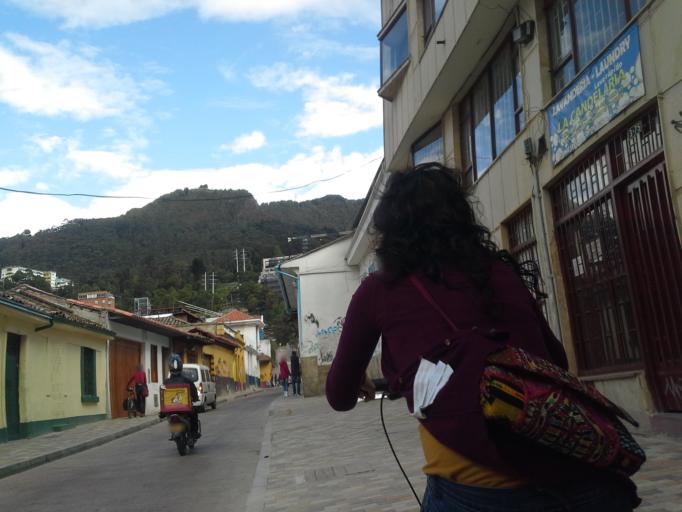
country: CO
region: Bogota D.C.
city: Bogota
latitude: 4.6000
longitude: -74.0702
